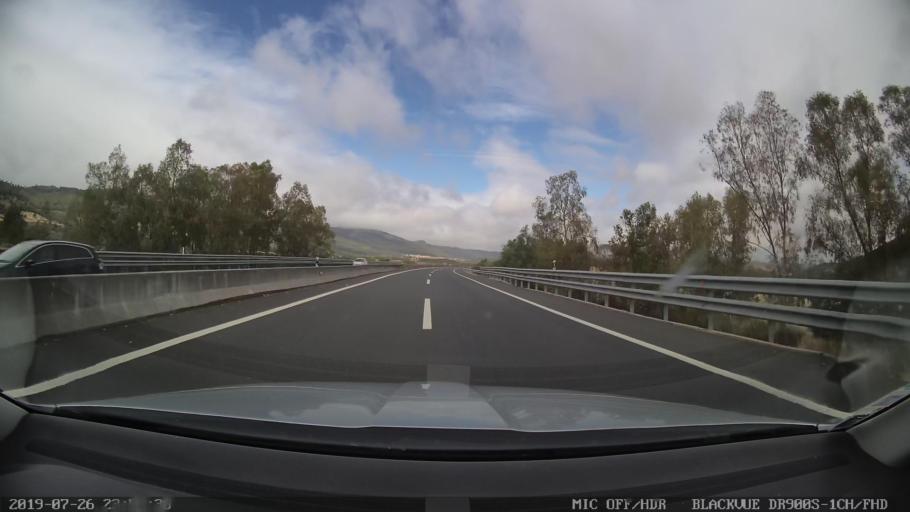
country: ES
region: Extremadura
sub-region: Provincia de Caceres
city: Romangordo
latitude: 39.7152
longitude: -5.7036
